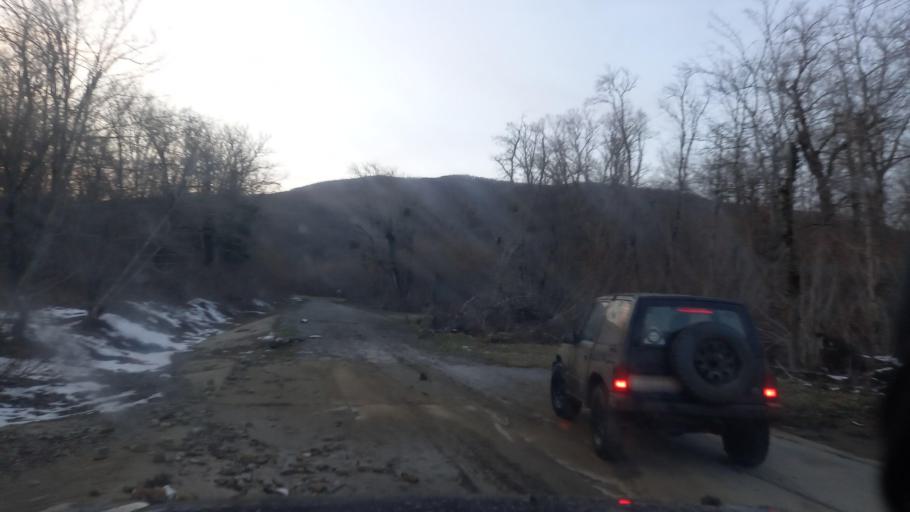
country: RU
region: Krasnodarskiy
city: Smolenskaya
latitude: 44.6225
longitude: 38.8241
